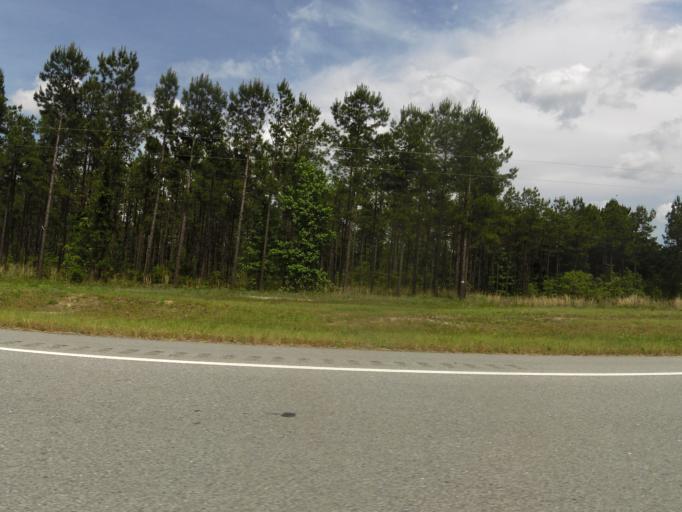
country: US
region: Georgia
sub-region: Jefferson County
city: Wadley
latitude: 32.7734
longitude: -82.3833
